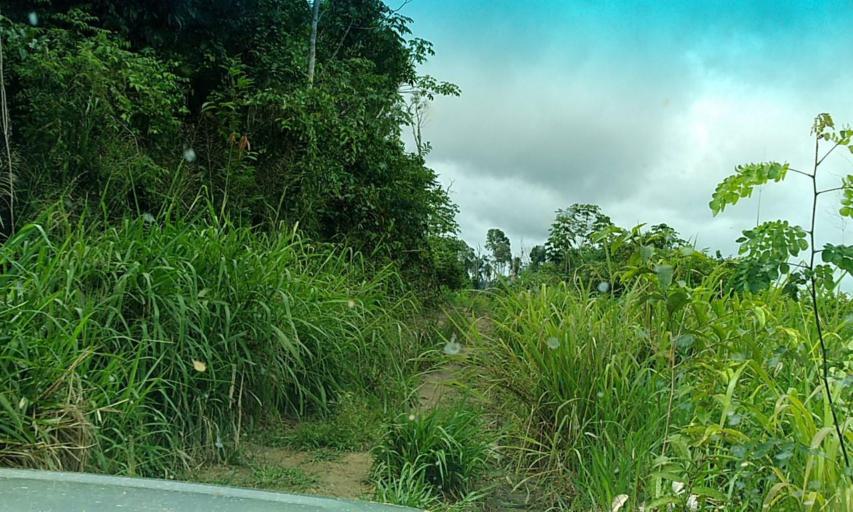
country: BR
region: Para
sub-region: Senador Jose Porfirio
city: Senador Jose Porfirio
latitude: -3.0404
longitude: -51.7210
